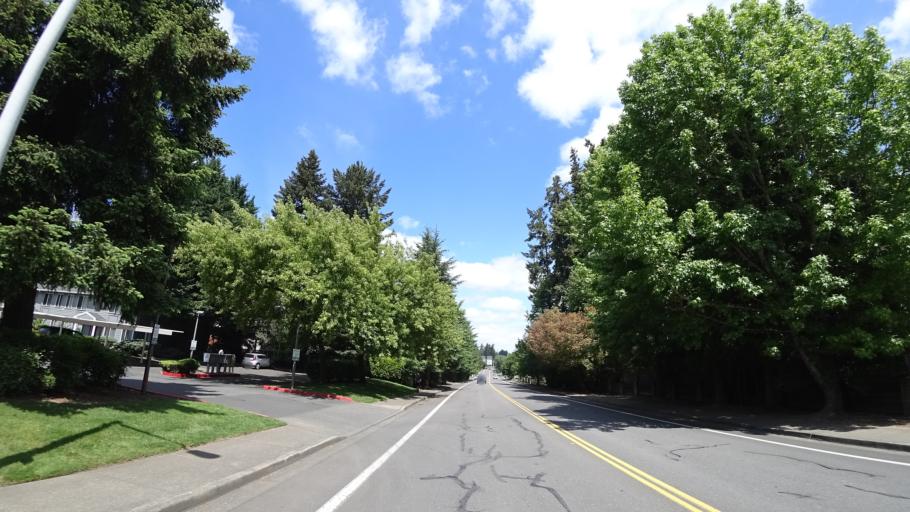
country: US
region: Oregon
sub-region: Washington County
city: King City
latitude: 45.4373
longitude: -122.8158
